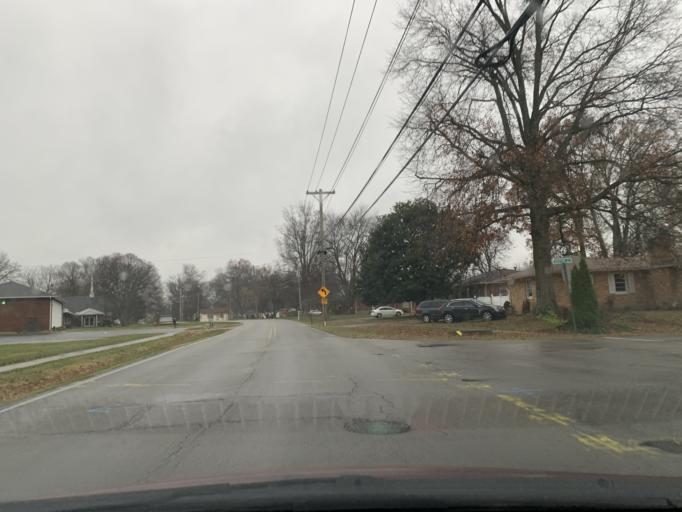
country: US
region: Kentucky
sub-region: Jefferson County
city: Buechel
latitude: 38.1987
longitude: -85.6422
